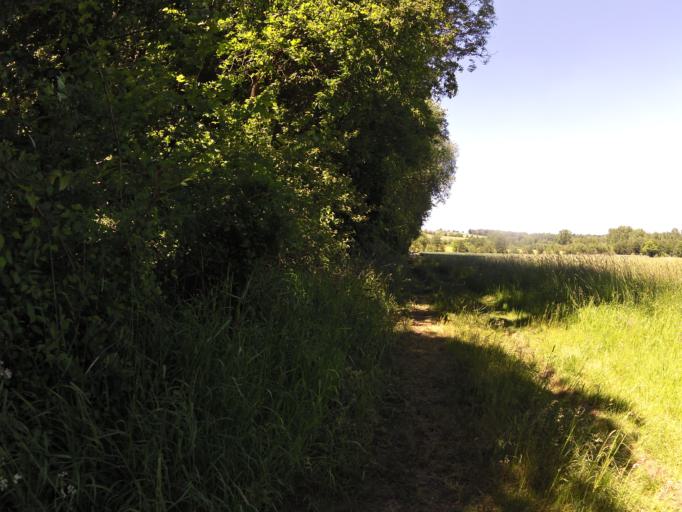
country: DE
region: Thuringia
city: Dankmarshausen
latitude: 50.9464
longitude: 10.0164
